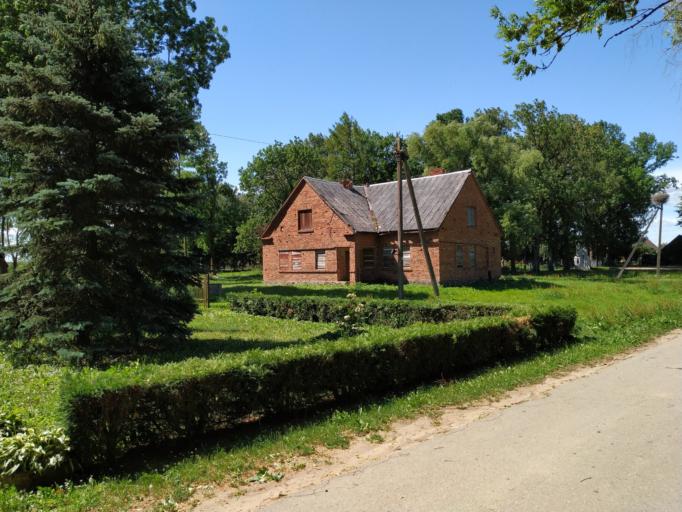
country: LT
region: Panevezys
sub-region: Birzai
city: Birzai
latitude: 56.2535
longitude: 24.5438
